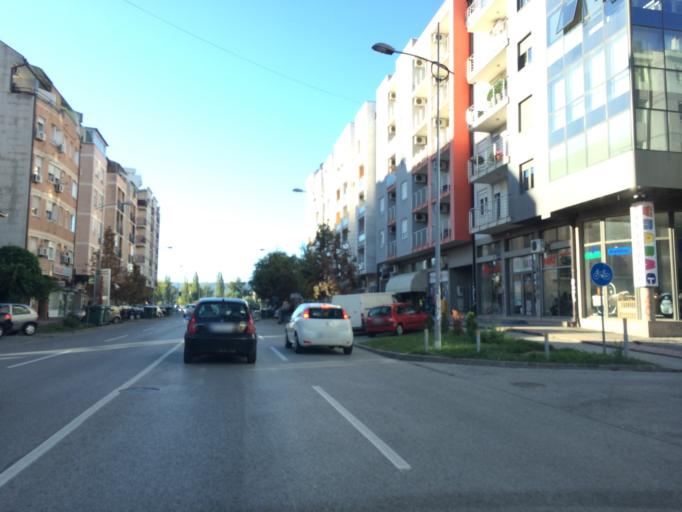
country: RS
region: Autonomna Pokrajina Vojvodina
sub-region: Juznobacki Okrug
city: Novi Sad
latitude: 45.2416
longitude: 19.8252
